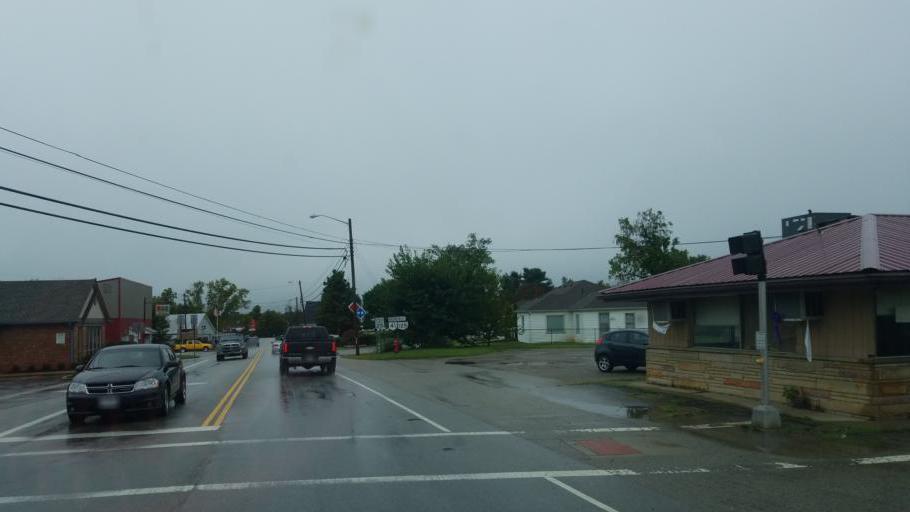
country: US
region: Ohio
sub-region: Adams County
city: West Union
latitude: 38.7959
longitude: -83.5367
